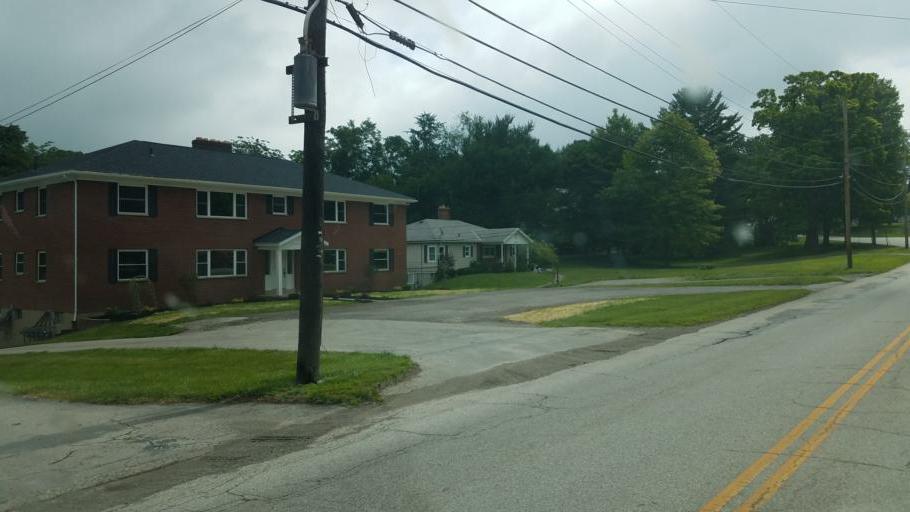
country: US
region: Ohio
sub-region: Highland County
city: Hillsboro
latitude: 39.2011
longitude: -83.6049
